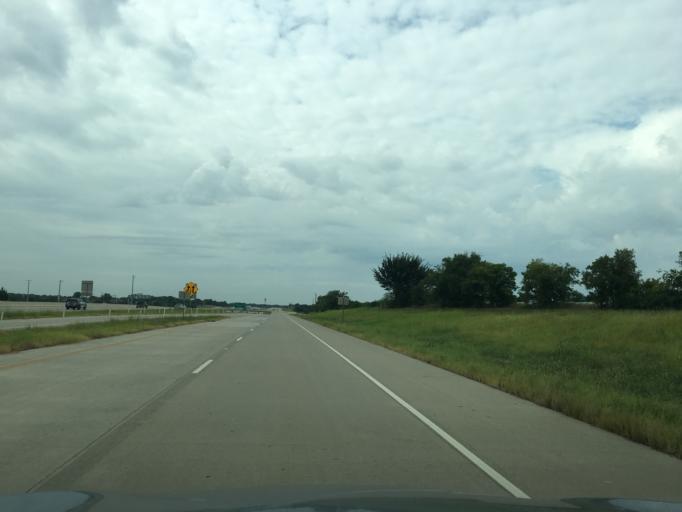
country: US
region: Texas
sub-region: Collin County
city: Melissa
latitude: 33.2908
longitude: -96.5925
